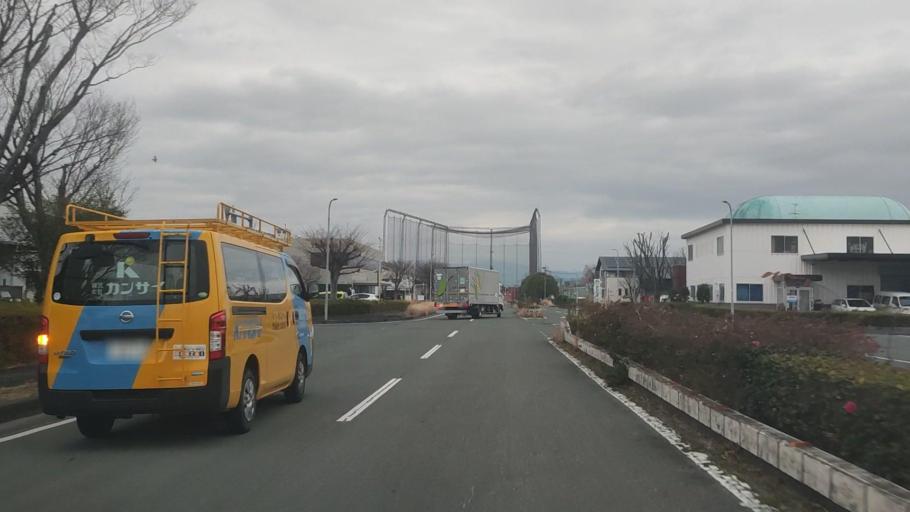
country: JP
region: Kumamoto
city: Kumamoto
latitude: 32.7668
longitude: 130.7054
